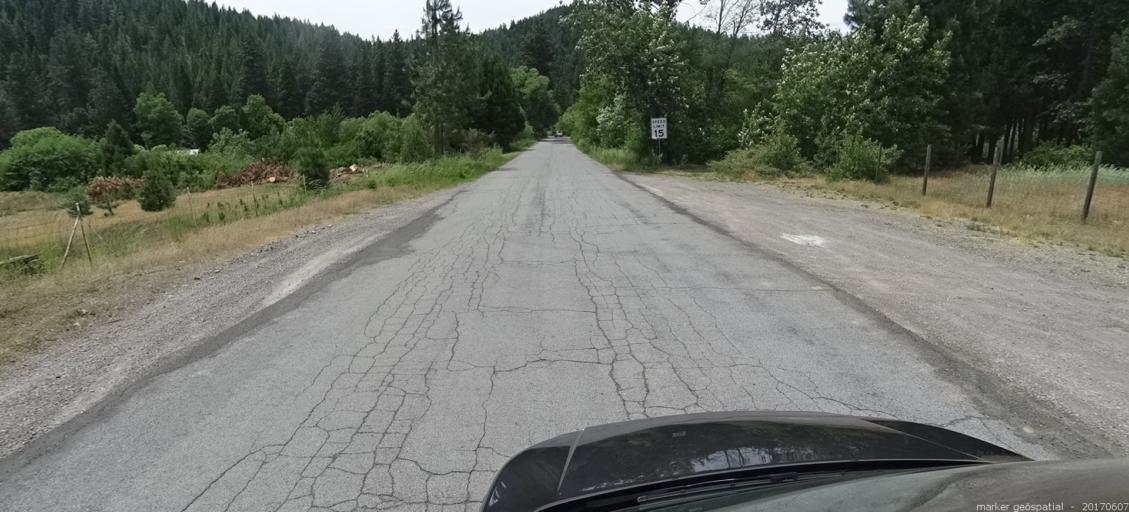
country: US
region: California
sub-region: Siskiyou County
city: Mount Shasta
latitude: 41.2941
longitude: -122.3236
